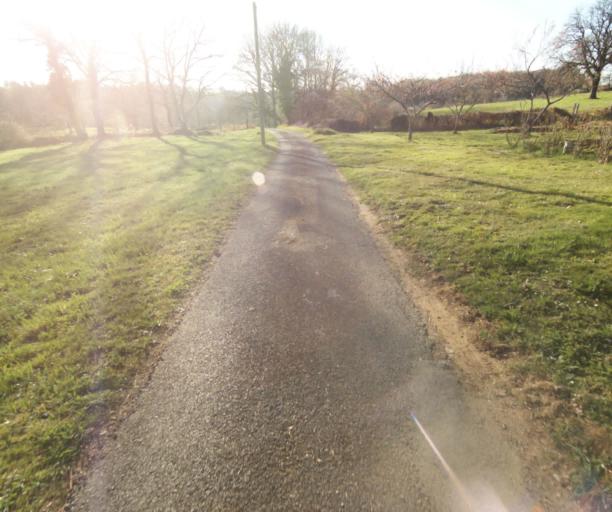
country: FR
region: Limousin
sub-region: Departement de la Correze
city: Seilhac
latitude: 45.3562
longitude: 1.7047
